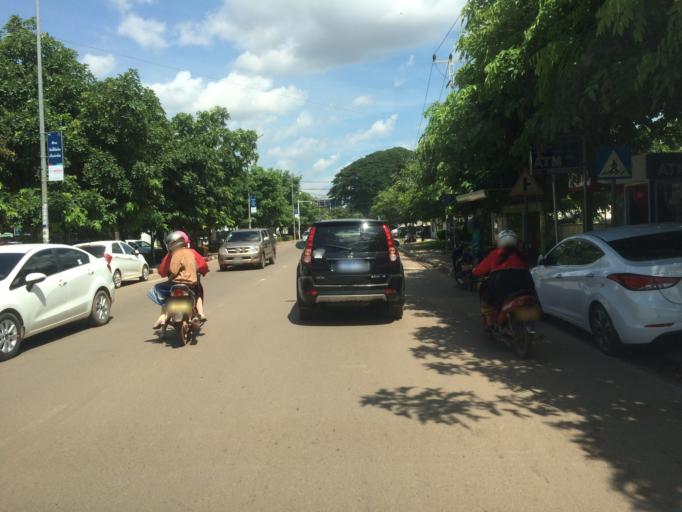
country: LA
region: Vientiane
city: Vientiane
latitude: 17.9693
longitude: 102.6084
